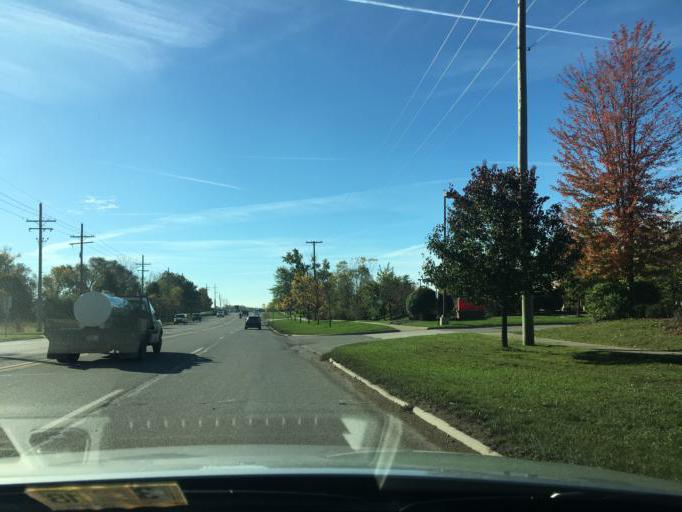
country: US
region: Michigan
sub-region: Wayne County
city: Plymouth
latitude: 42.3938
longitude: -83.5103
